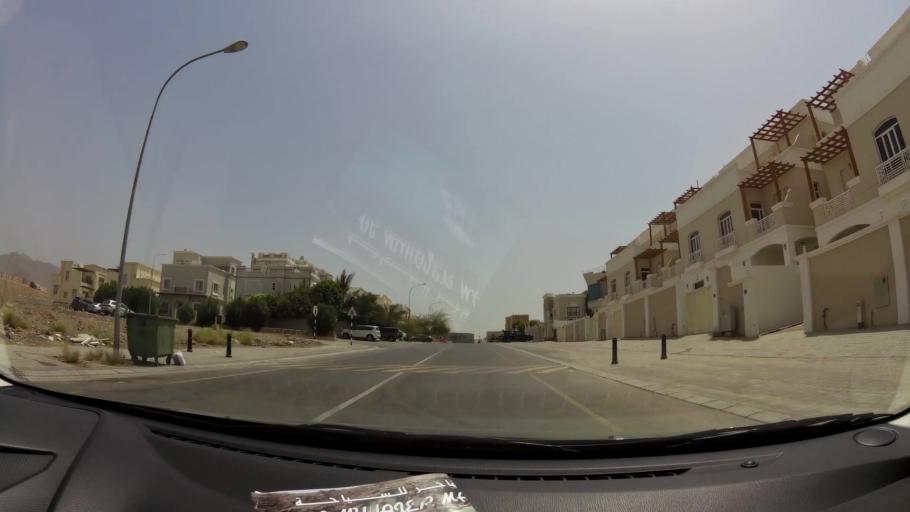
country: OM
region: Muhafazat Masqat
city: Bawshar
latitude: 23.5649
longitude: 58.3984
